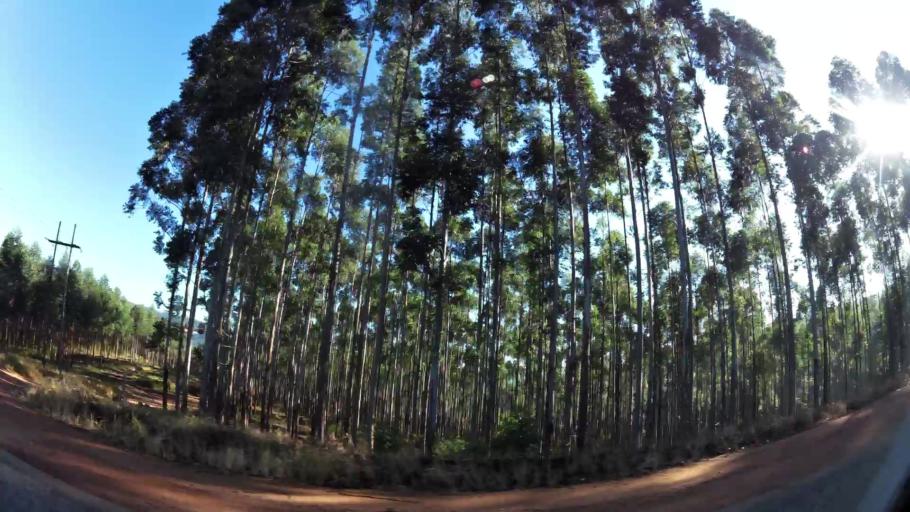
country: ZA
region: Limpopo
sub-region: Mopani District Municipality
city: Tzaneen
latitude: -23.8694
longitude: 30.1028
